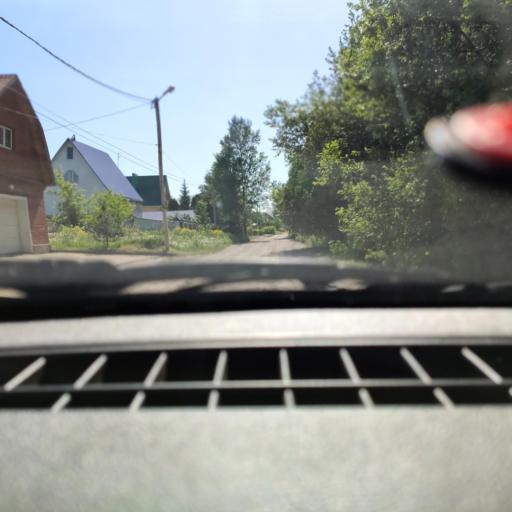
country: RU
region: Bashkortostan
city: Ufa
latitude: 54.6066
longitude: 55.9494
